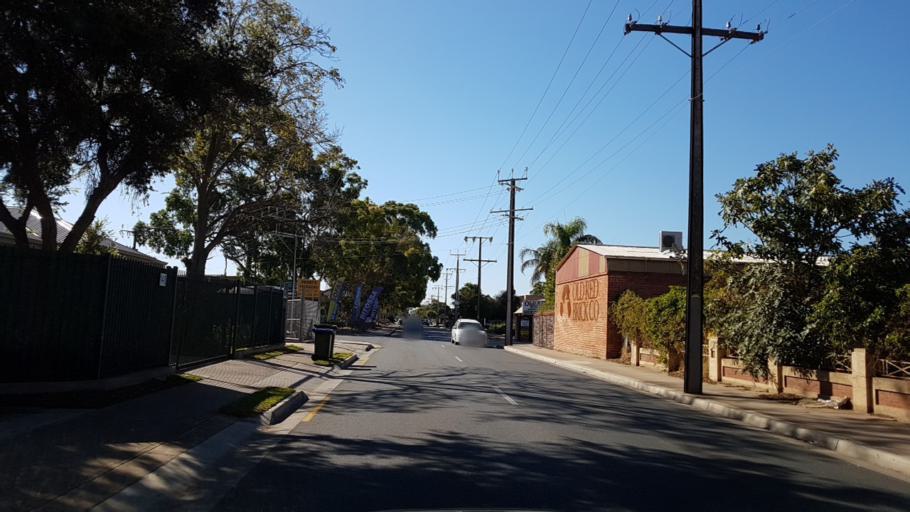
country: AU
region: South Australia
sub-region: Charles Sturt
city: Allenby Gardens
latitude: -34.9036
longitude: 138.5476
